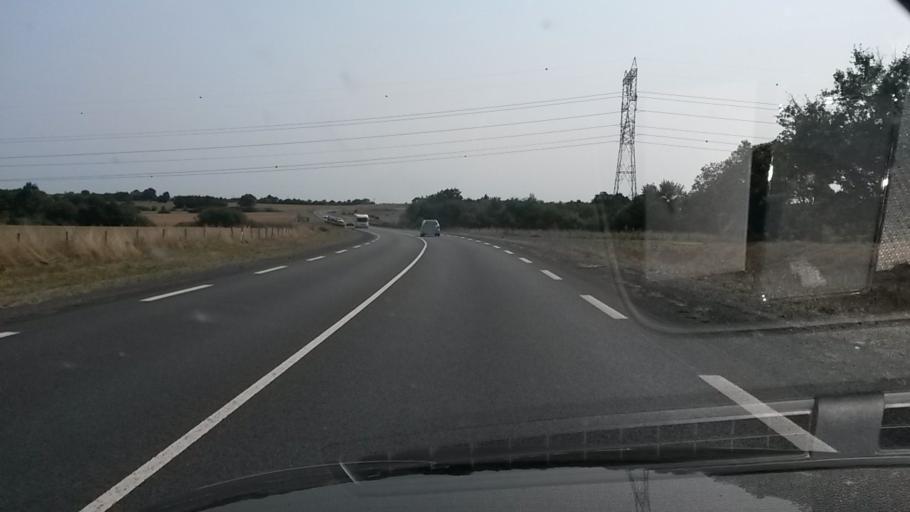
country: FR
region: Pays de la Loire
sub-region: Departement de la Loire-Atlantique
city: Mesanger
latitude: 47.4248
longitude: -1.1871
